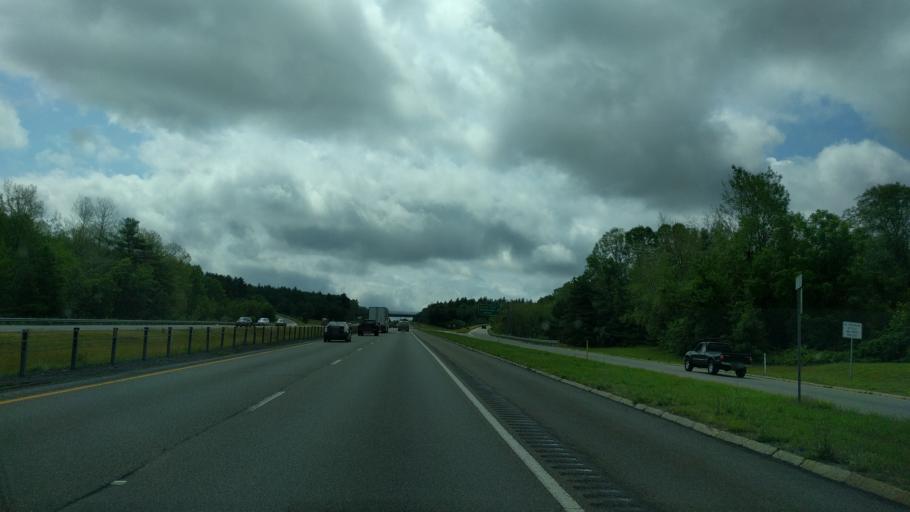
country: US
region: Massachusetts
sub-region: Worcester County
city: Sutton
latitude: 42.1538
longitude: -71.7270
